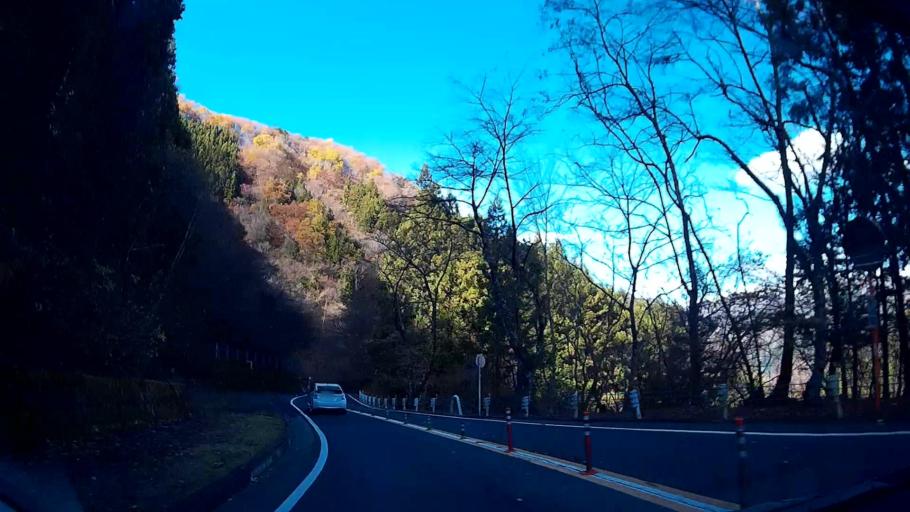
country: JP
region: Yamanashi
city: Uenohara
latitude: 35.7560
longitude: 139.0254
